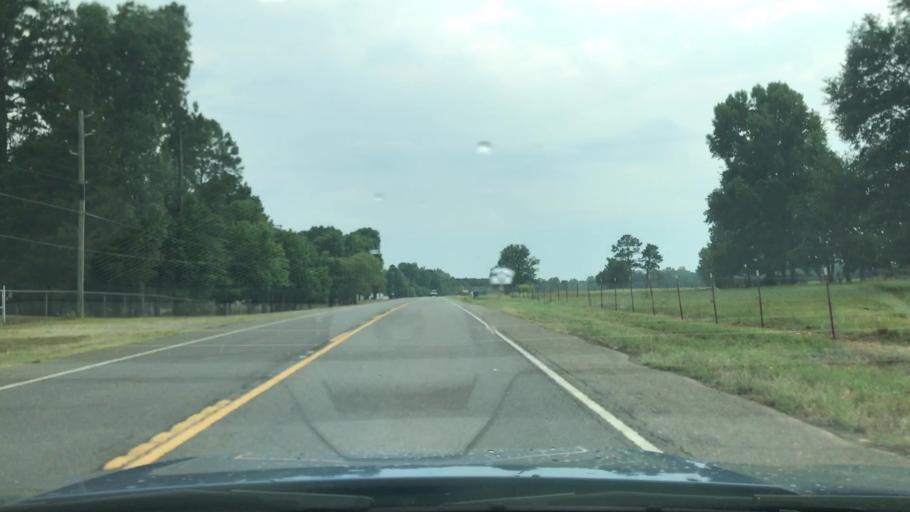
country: US
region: Texas
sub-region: Harrison County
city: Waskom
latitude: 32.4595
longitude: -94.0222
